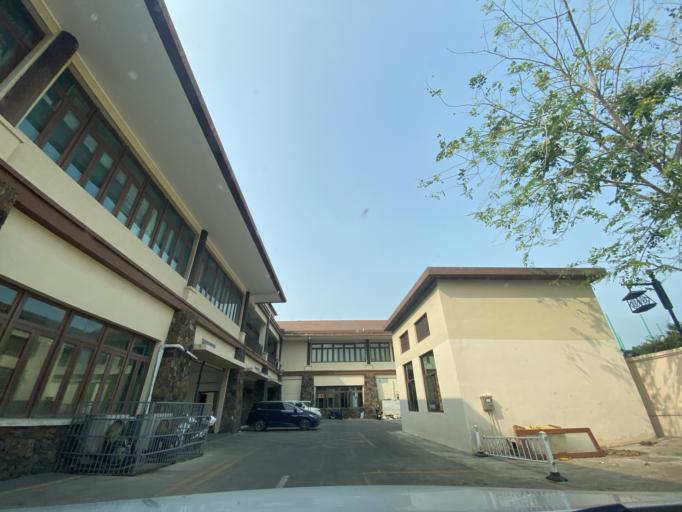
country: CN
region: Hainan
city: Yingzhou
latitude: 18.4018
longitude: 109.8472
